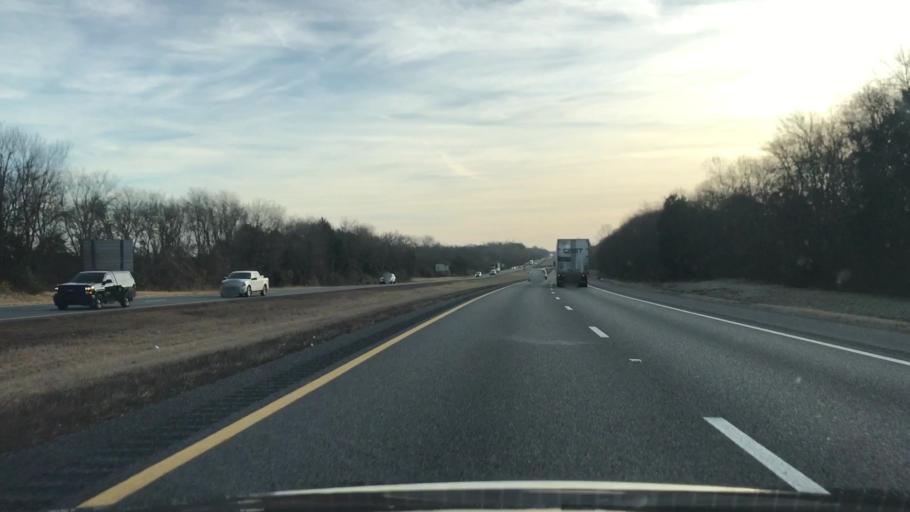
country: US
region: Tennessee
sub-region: Wilson County
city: Lebanon
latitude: 36.1925
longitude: -86.2440
